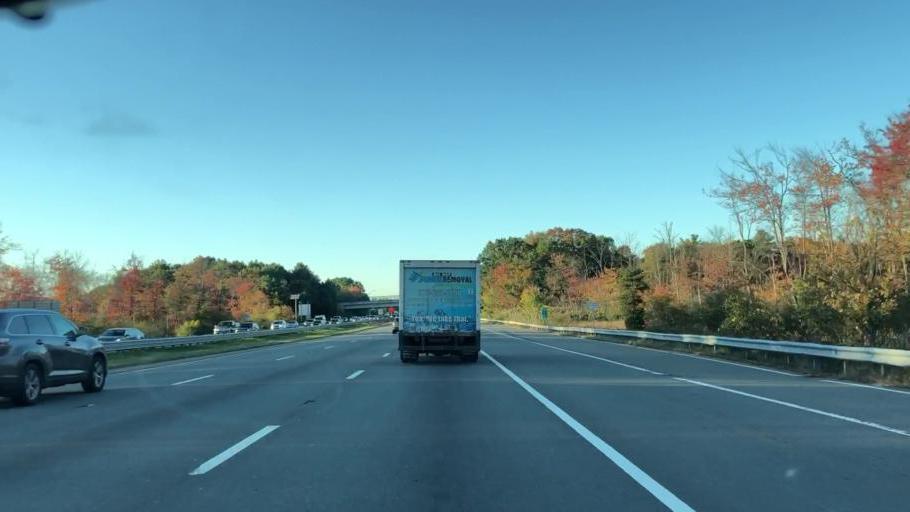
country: US
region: Massachusetts
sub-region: Essex County
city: Andover
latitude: 42.6564
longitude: -71.1906
